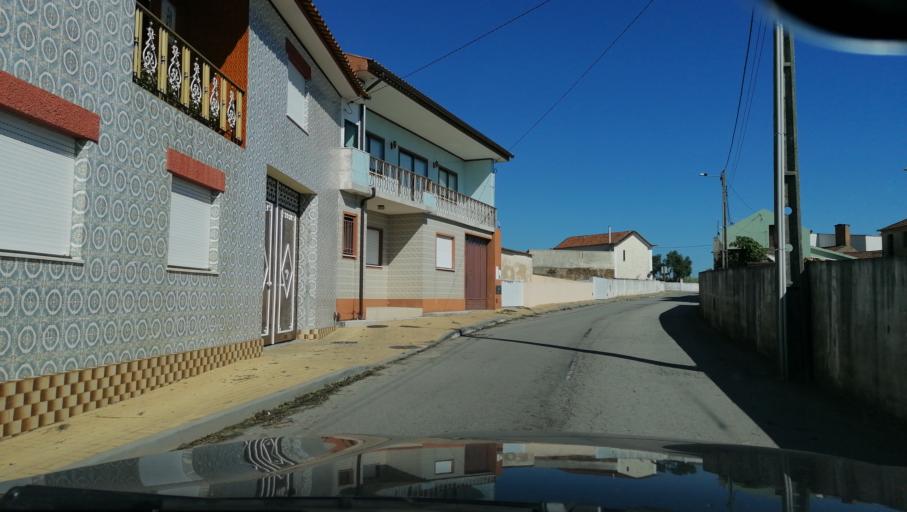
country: PT
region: Aveiro
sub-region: Estarreja
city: Salreu
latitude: 40.7490
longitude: -8.5514
